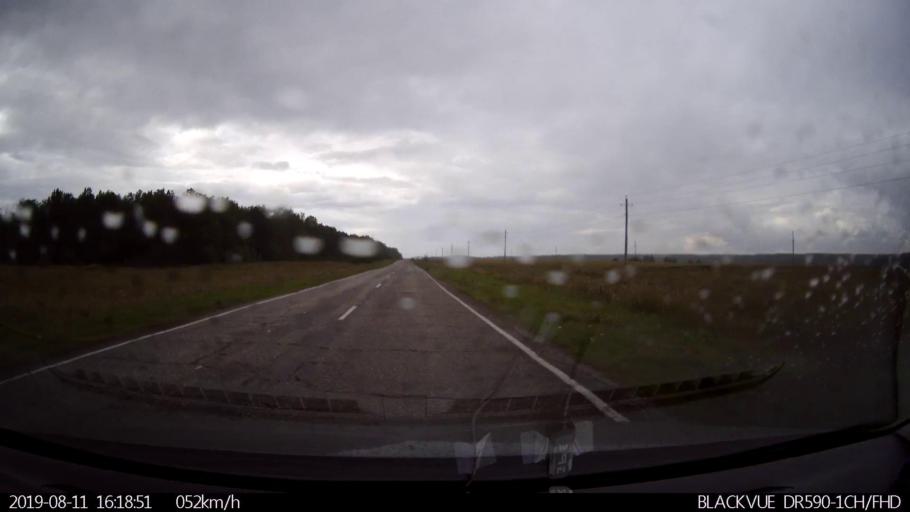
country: RU
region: Ulyanovsk
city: Mayna
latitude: 54.0585
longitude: 47.6101
